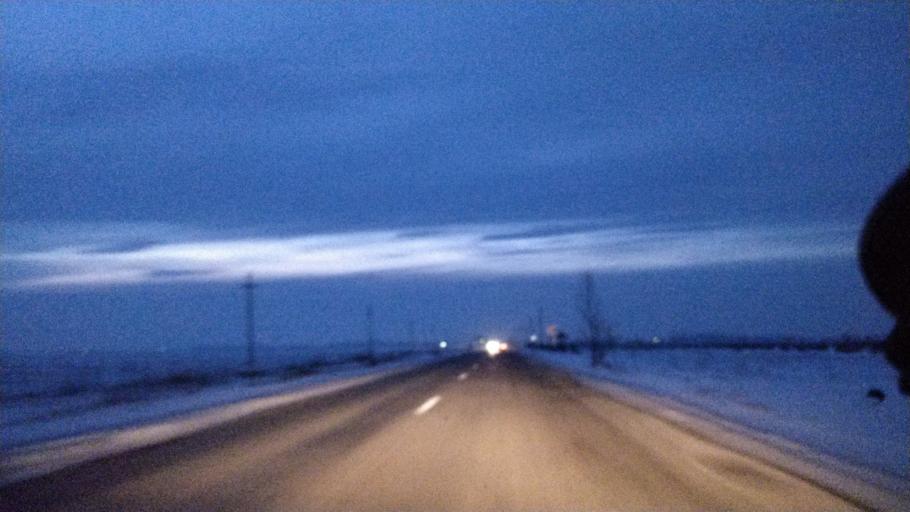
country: RO
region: Vrancea
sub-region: Comuna Rastoaca
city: Rastoaca
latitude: 45.6516
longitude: 27.3106
